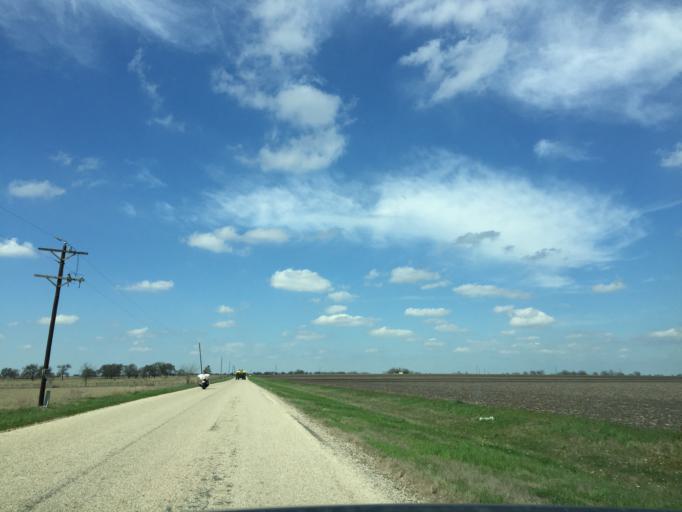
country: US
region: Texas
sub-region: Milam County
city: Thorndale
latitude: 30.5429
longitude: -97.2708
